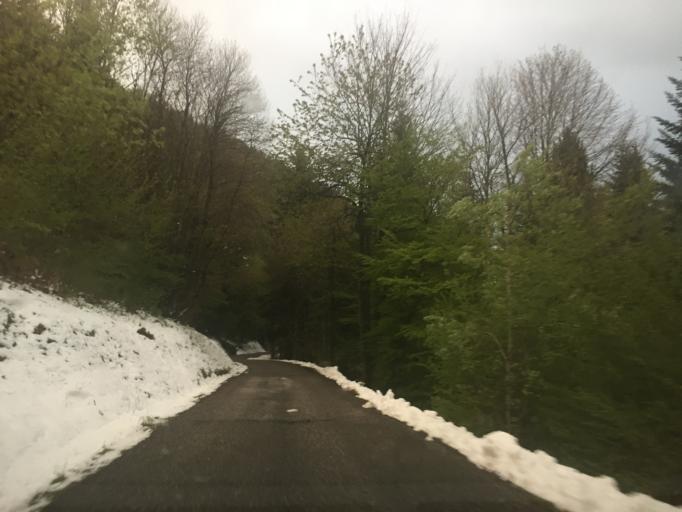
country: FR
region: Rhone-Alpes
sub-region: Departement de la Savoie
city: La Motte-Servolex
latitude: 45.5887
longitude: 5.8282
